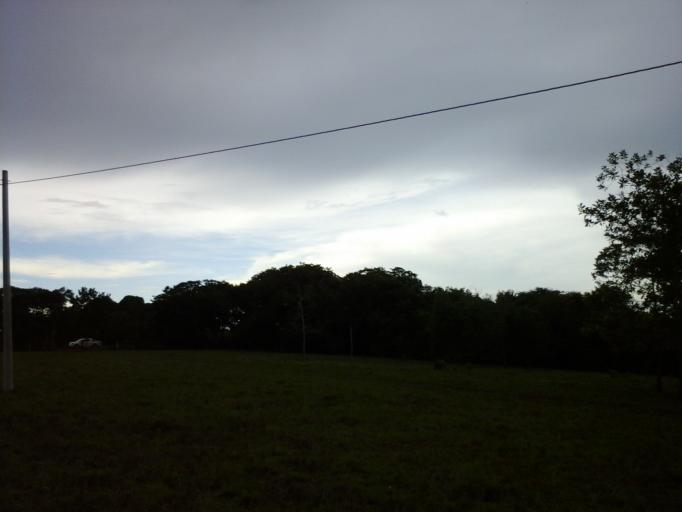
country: CO
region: Cundinamarca
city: Tibacuy
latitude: 4.1907
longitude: -72.4334
